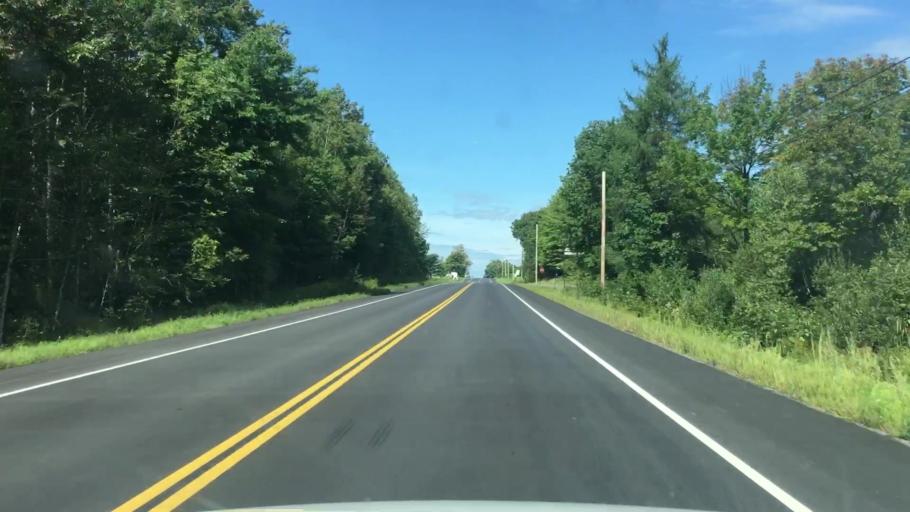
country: US
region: Maine
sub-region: Penobscot County
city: Corinna
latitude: 44.9511
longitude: -69.2518
